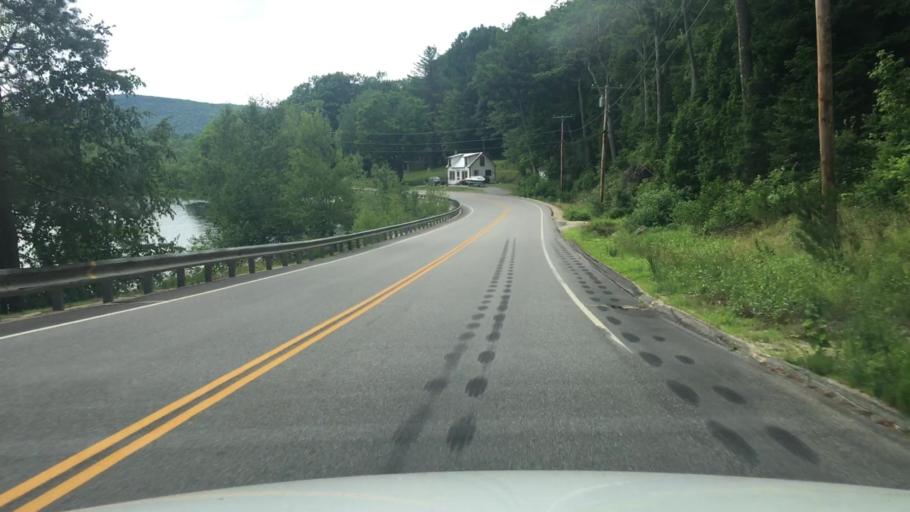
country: US
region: Maine
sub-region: Oxford County
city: Paris
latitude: 44.3700
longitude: -70.4660
